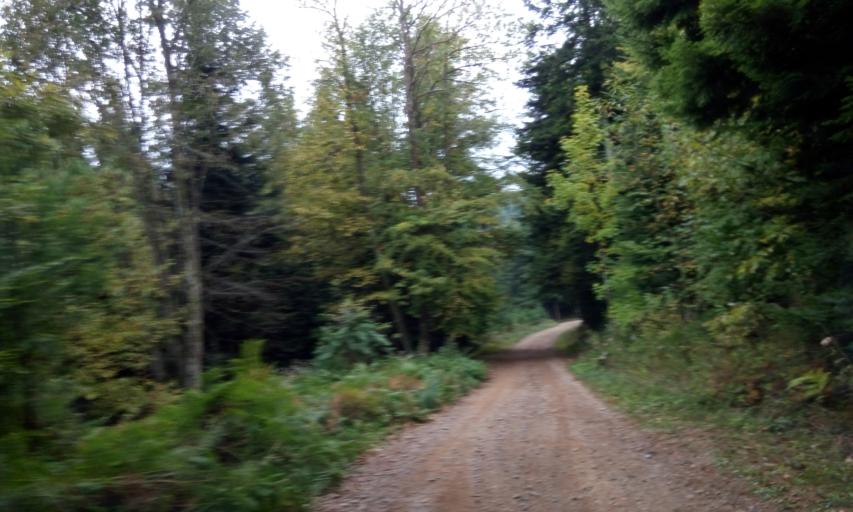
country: FR
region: Rhone-Alpes
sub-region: Departement du Rhone
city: Cublize
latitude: 46.0125
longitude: 4.4236
